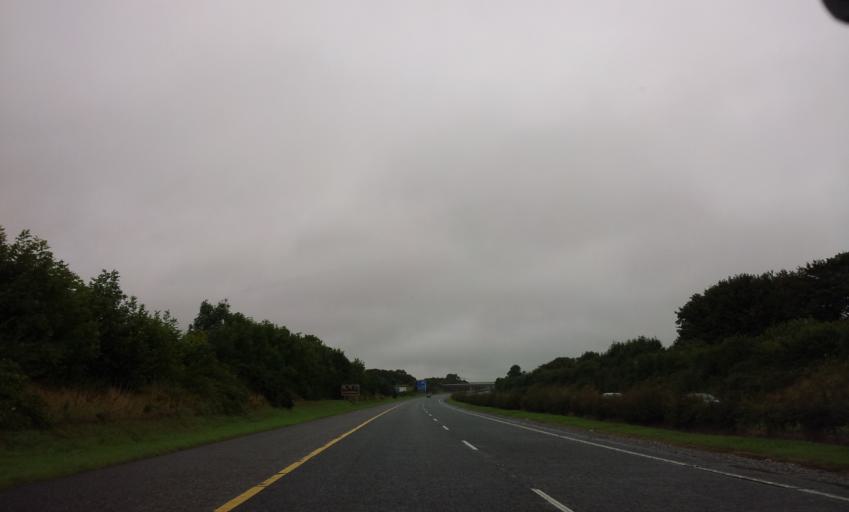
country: IE
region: Munster
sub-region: County Cork
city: Watergrasshill
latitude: 51.9916
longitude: -8.3597
